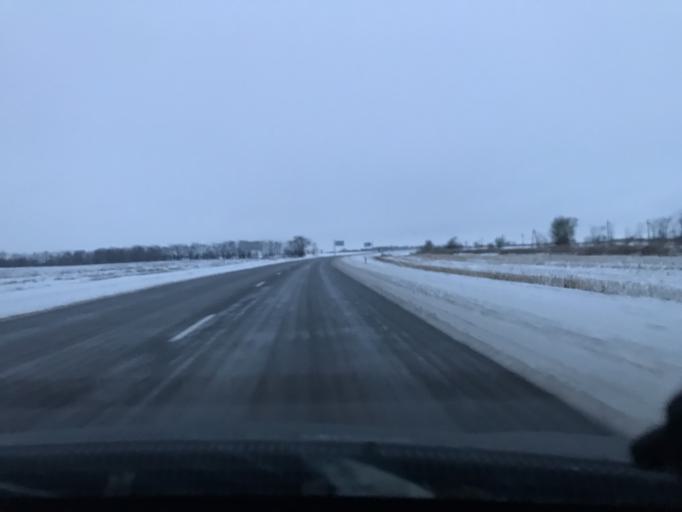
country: RU
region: Rostov
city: Letnik
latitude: 45.9551
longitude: 41.2796
